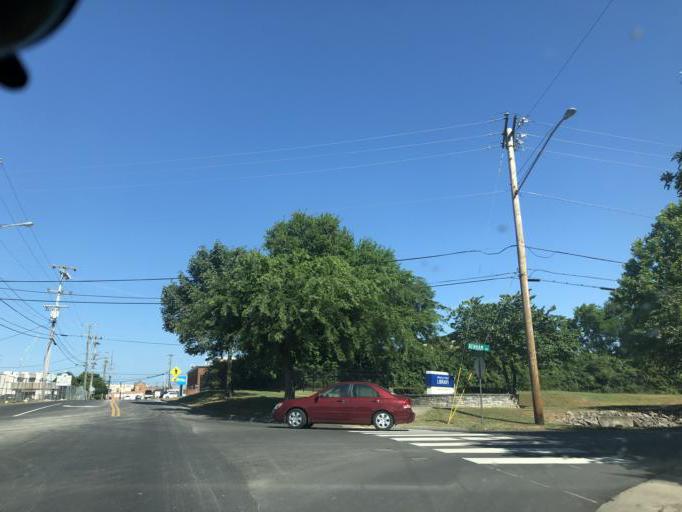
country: US
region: Tennessee
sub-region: Davidson County
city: Oak Hill
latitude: 36.1080
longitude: -86.8093
